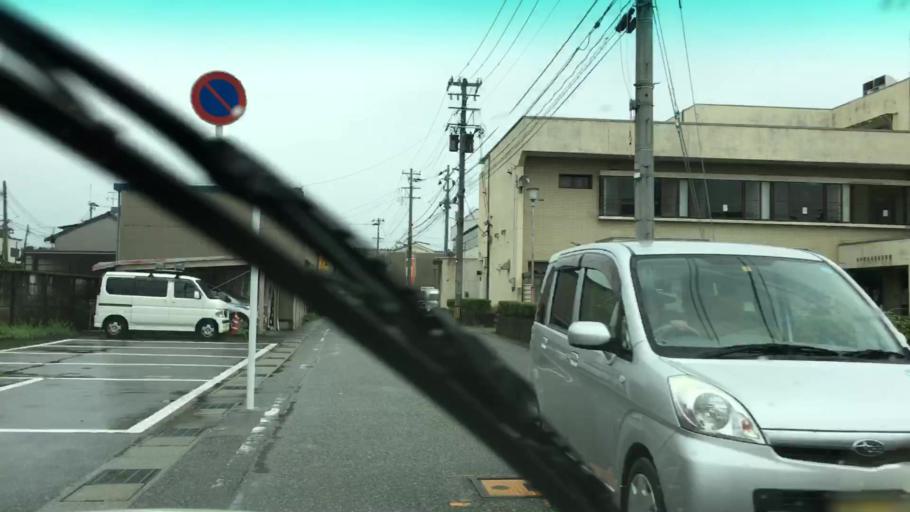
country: JP
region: Toyama
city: Kamiichi
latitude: 36.6640
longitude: 137.3159
